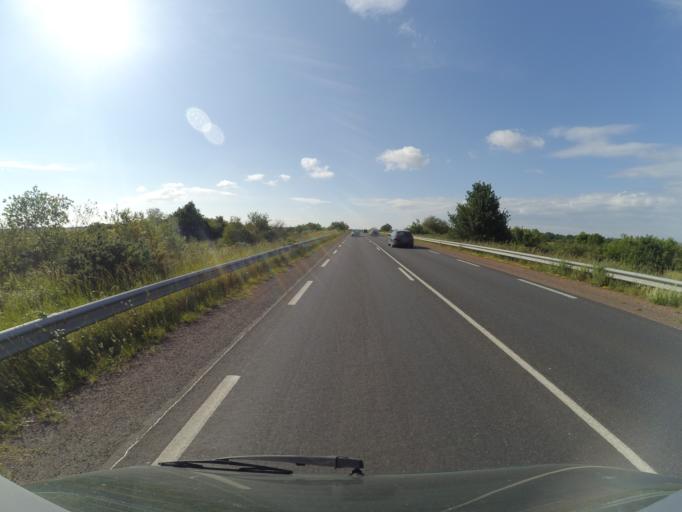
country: FR
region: Poitou-Charentes
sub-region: Departement de la Charente-Maritime
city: Saint-Agnant
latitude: 45.8545
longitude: -0.9618
